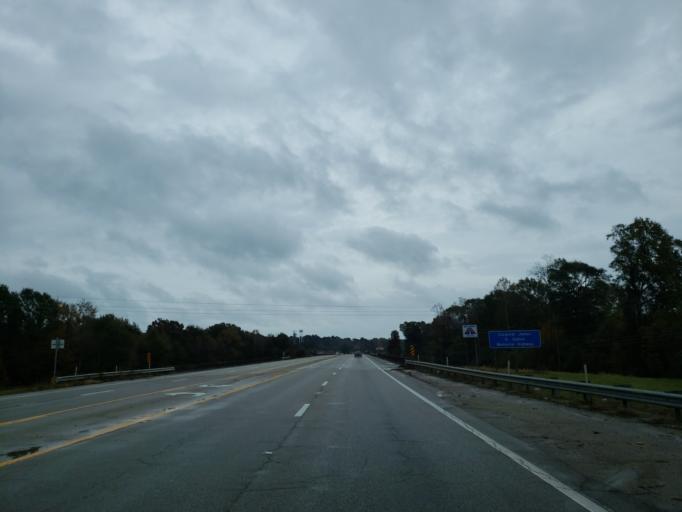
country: US
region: Mississippi
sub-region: Jones County
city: Laurel
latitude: 31.6976
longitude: -89.1128
